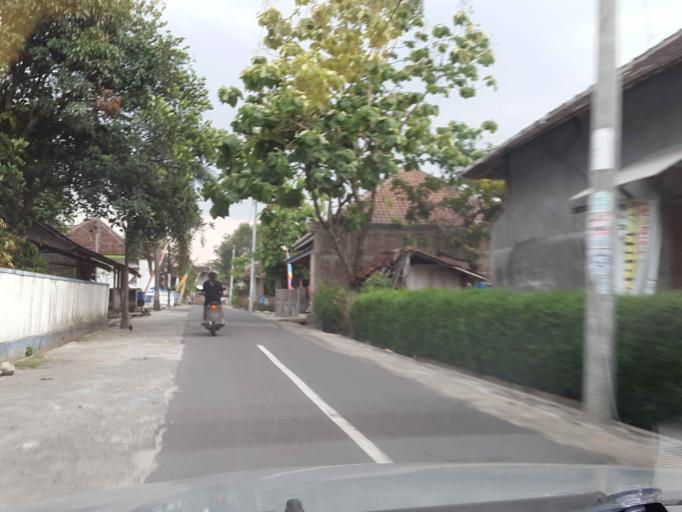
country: ID
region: Central Java
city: Jaten
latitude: -7.5968
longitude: 110.9413
